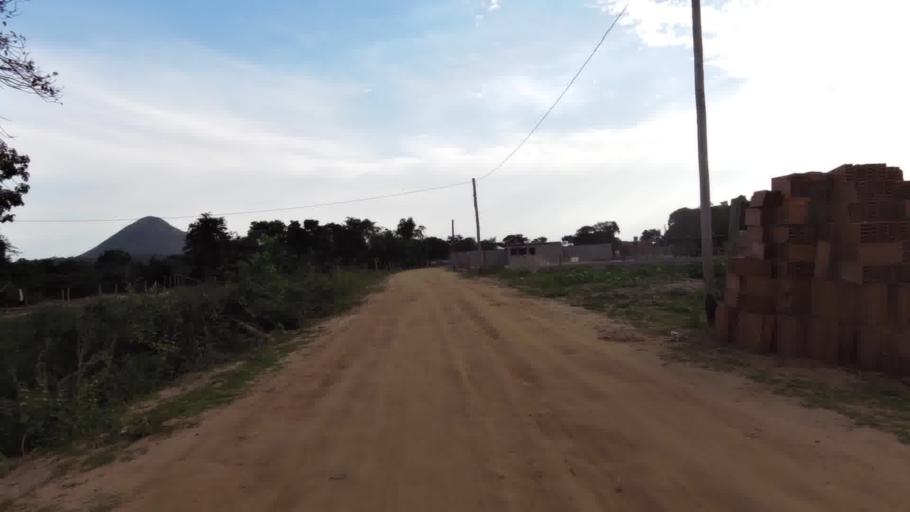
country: BR
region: Espirito Santo
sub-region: Piuma
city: Piuma
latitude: -20.8429
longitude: -40.7524
